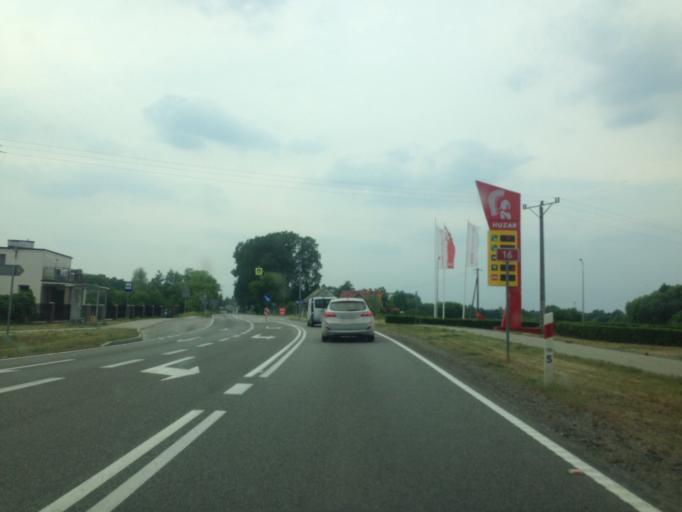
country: PL
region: Kujawsko-Pomorskie
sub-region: Powiat grudziadzki
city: Rogozno
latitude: 53.5024
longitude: 18.8660
